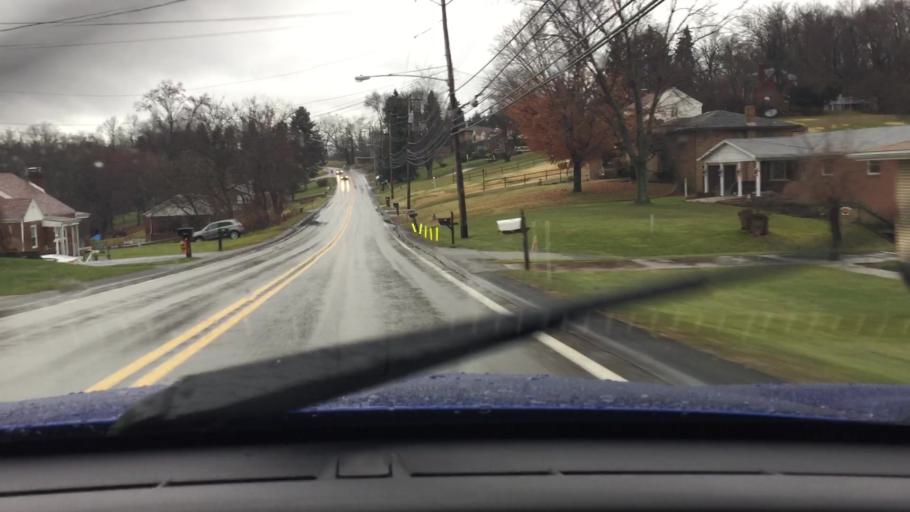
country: US
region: Pennsylvania
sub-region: Allegheny County
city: Wilson
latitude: 40.3129
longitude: -79.9168
